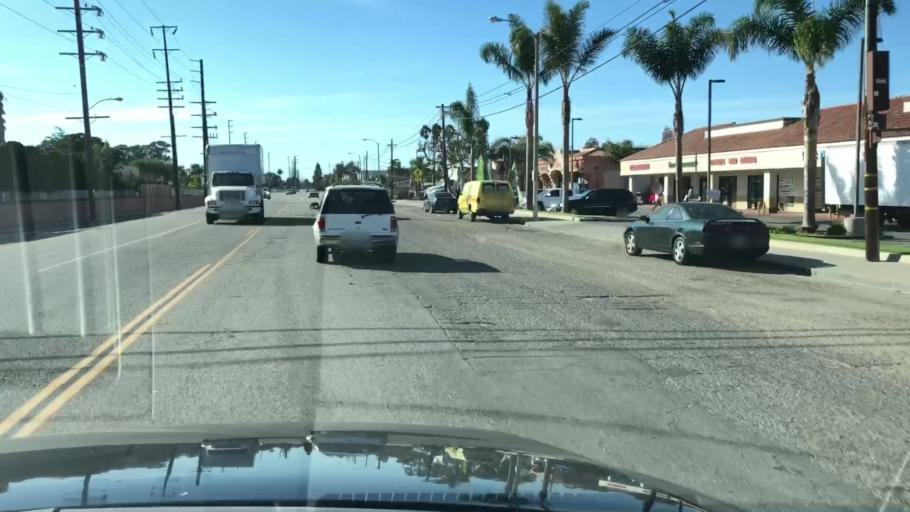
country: US
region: California
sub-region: Ventura County
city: Oxnard
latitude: 34.1733
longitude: -119.1496
